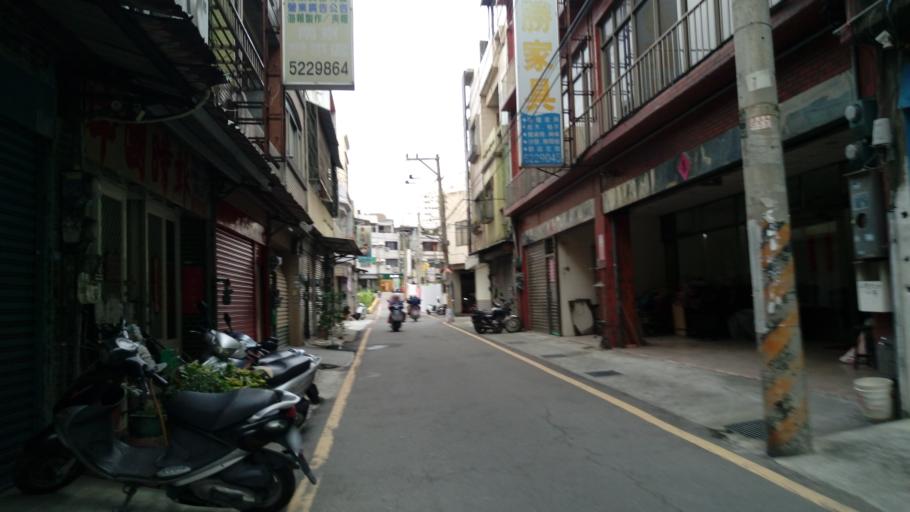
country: TW
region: Taiwan
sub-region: Hsinchu
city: Hsinchu
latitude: 24.8040
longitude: 120.9522
